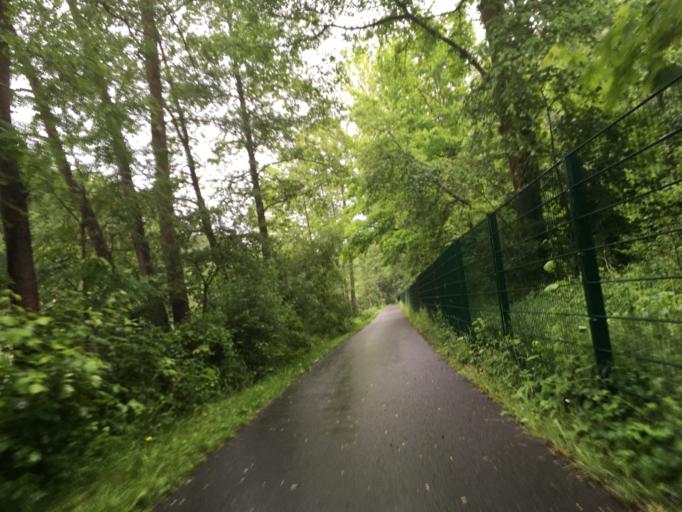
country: DE
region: Brandenburg
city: Eberswalde
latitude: 52.8452
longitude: 13.7729
